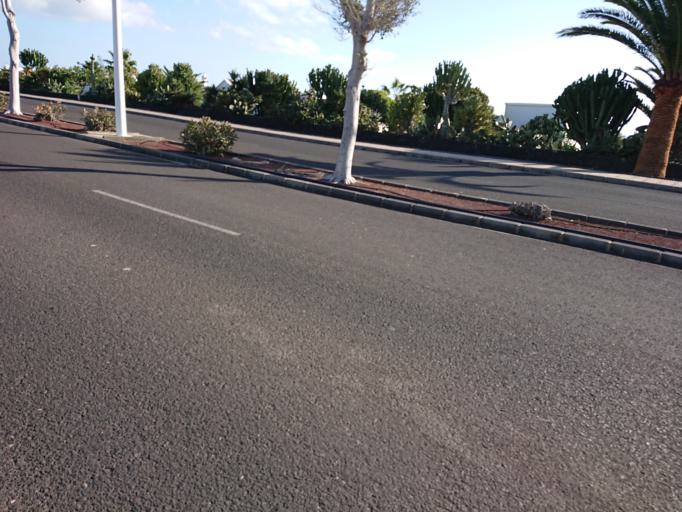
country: ES
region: Canary Islands
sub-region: Provincia de Las Palmas
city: Playa Blanca
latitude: 28.8655
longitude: -13.8481
